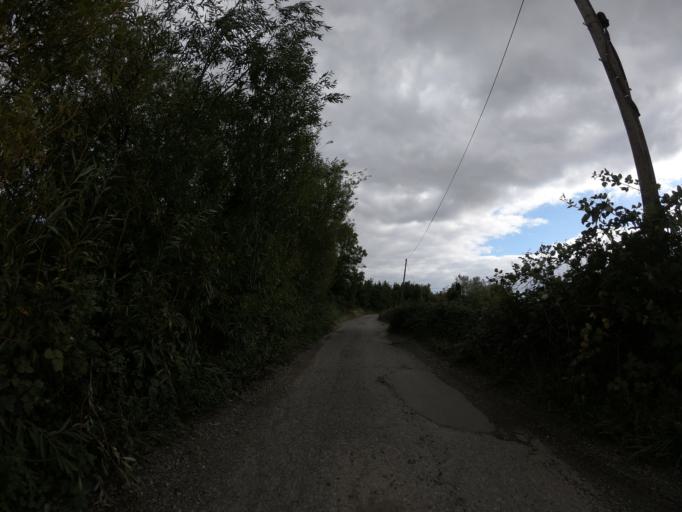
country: GB
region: England
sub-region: Kent
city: Dartford
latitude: 51.4676
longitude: 0.2162
